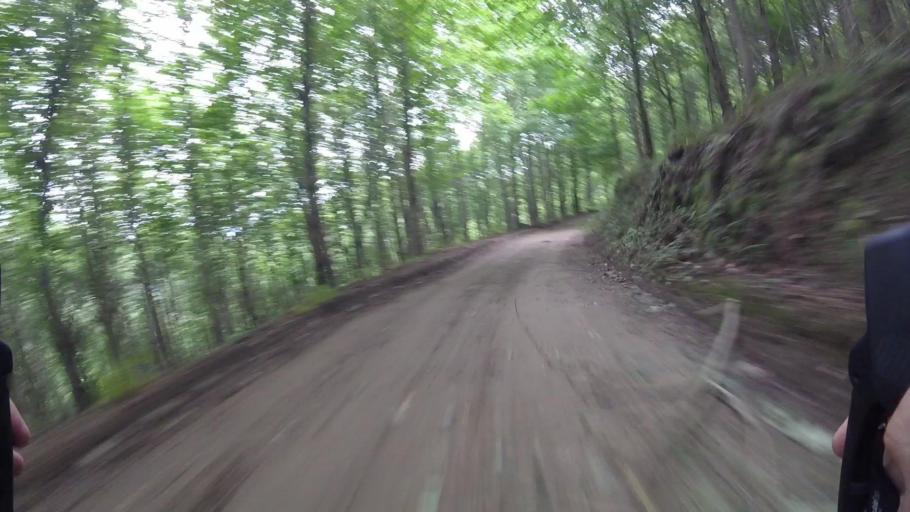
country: ES
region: Basque Country
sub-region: Provincia de Guipuzcoa
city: Errenteria
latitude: 43.2602
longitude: -1.8529
